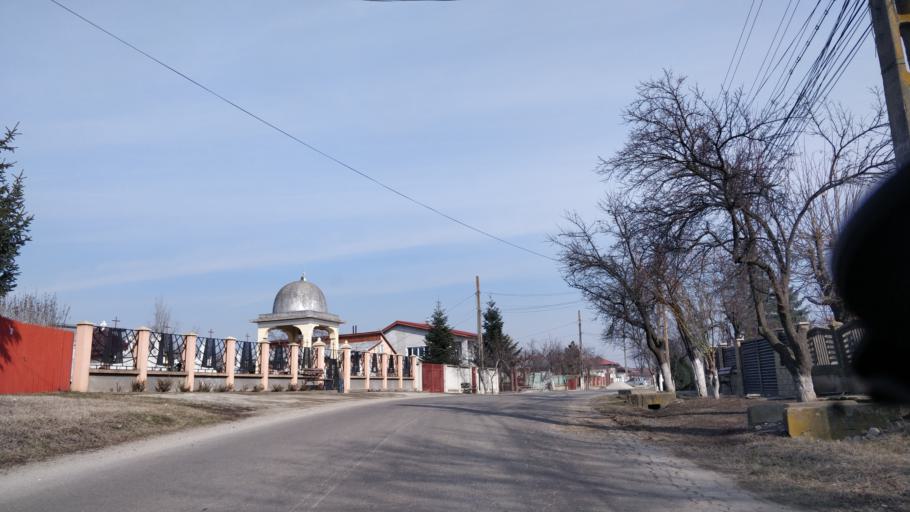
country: RO
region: Giurgiu
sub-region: Comuna Ulmi
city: Ulmi
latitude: 44.4858
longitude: 25.7782
